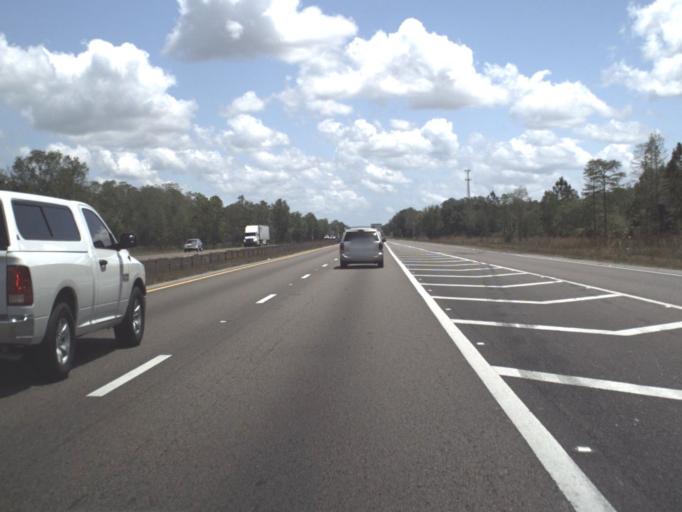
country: US
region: Florida
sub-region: Orange County
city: Wedgefield
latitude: 28.4515
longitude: -81.1554
